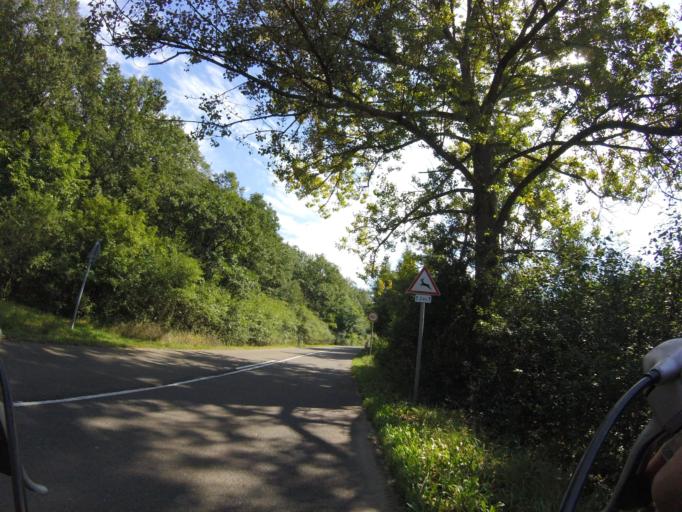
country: HU
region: Komarom-Esztergom
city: Esztergom
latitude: 47.8665
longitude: 18.7926
